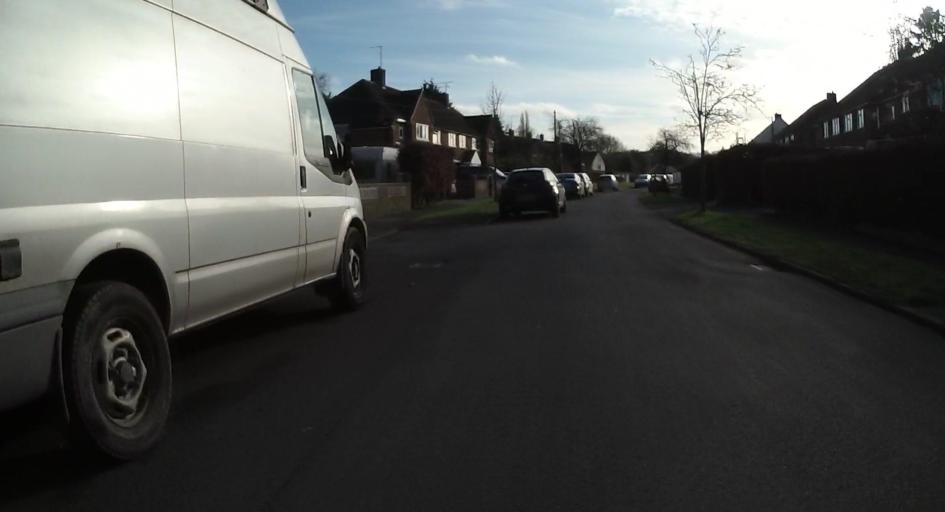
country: GB
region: England
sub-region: Wokingham
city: Wokingham
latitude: 51.4017
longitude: -0.8393
